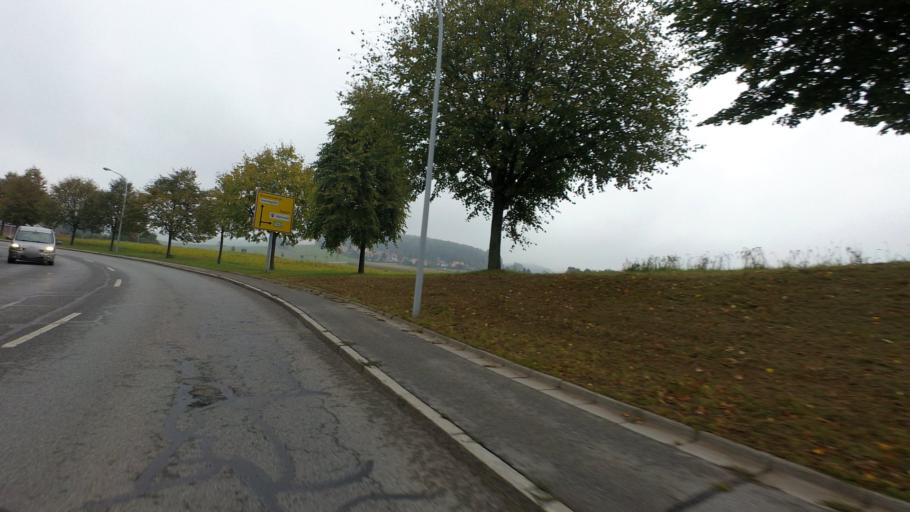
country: DE
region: Saxony
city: Neustadt in Sachsen
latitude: 51.0261
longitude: 14.2328
